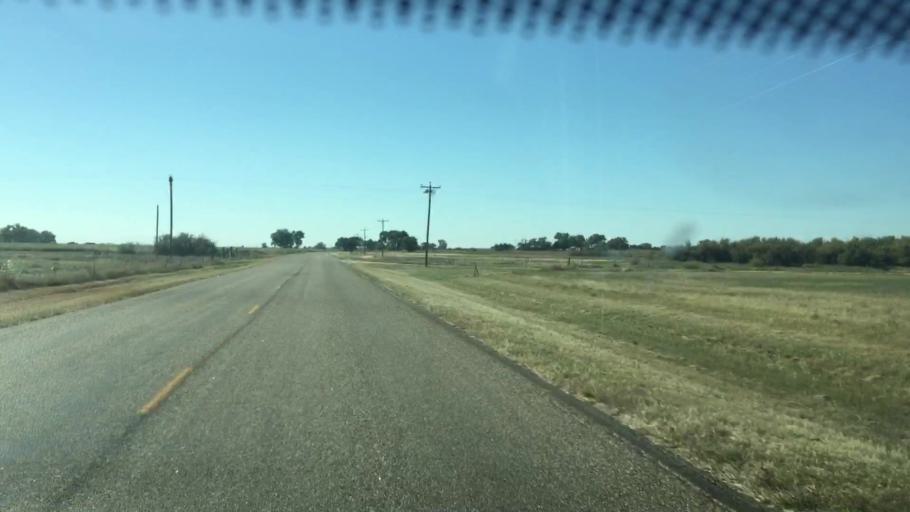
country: US
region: Colorado
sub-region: Prowers County
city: Lamar
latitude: 38.1146
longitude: -102.5753
